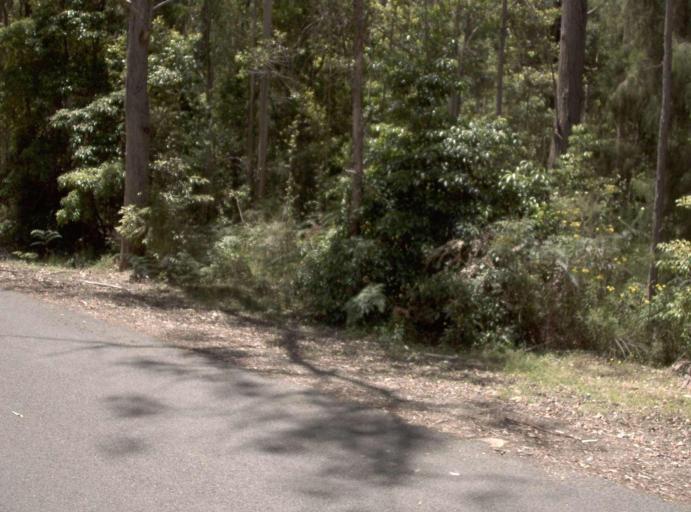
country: AU
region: New South Wales
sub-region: Bombala
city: Bombala
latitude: -37.4891
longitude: 148.9282
